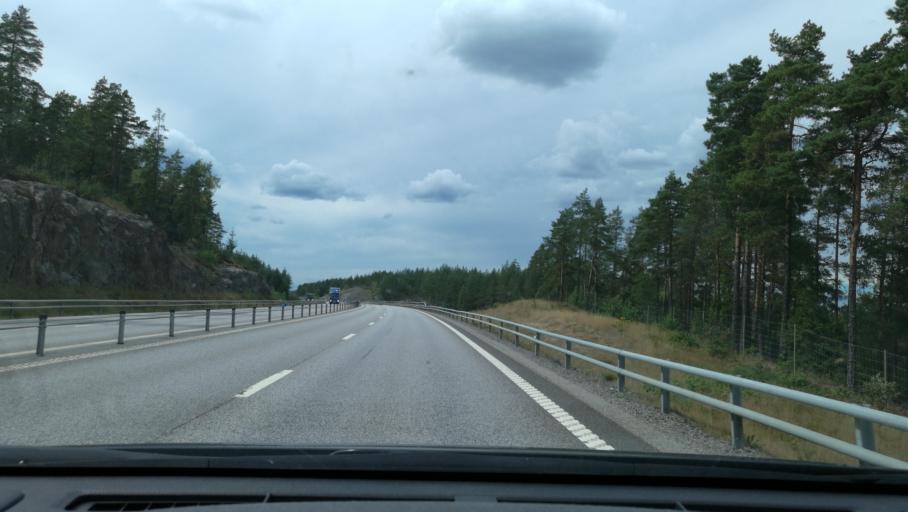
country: SE
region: OEstergoetland
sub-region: Norrkopings Kommun
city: Svartinge
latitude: 58.6615
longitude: 16.0338
